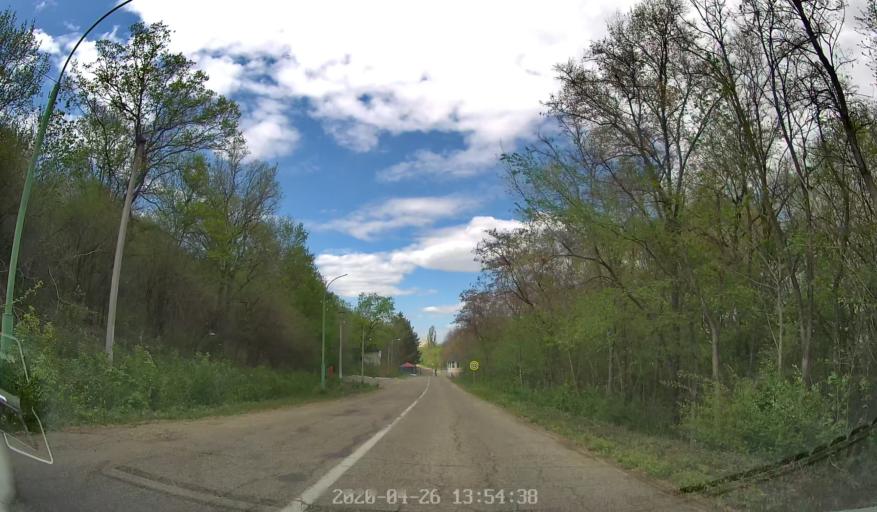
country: MD
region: Telenesti
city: Cocieri
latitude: 47.2868
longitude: 29.0999
